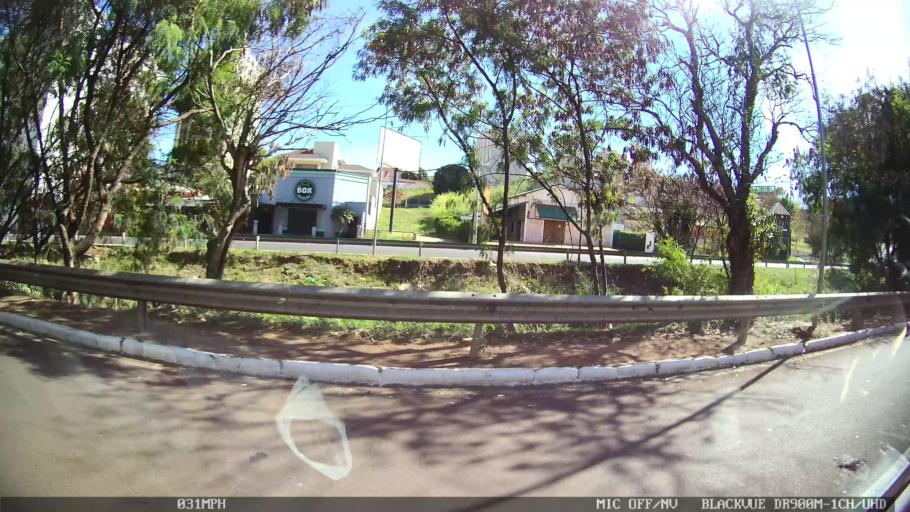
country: BR
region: Sao Paulo
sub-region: Franca
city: Franca
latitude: -20.5498
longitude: -47.4028
